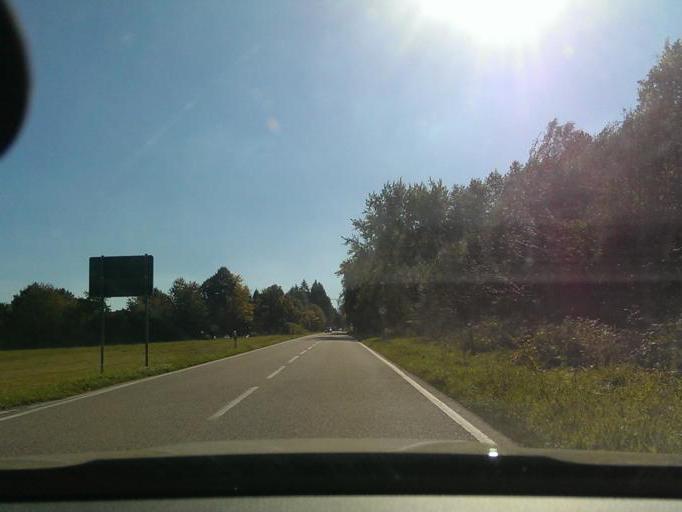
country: DE
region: Baden-Wuerttemberg
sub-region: Karlsruhe Region
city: Dobel
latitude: 48.8028
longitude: 8.4880
